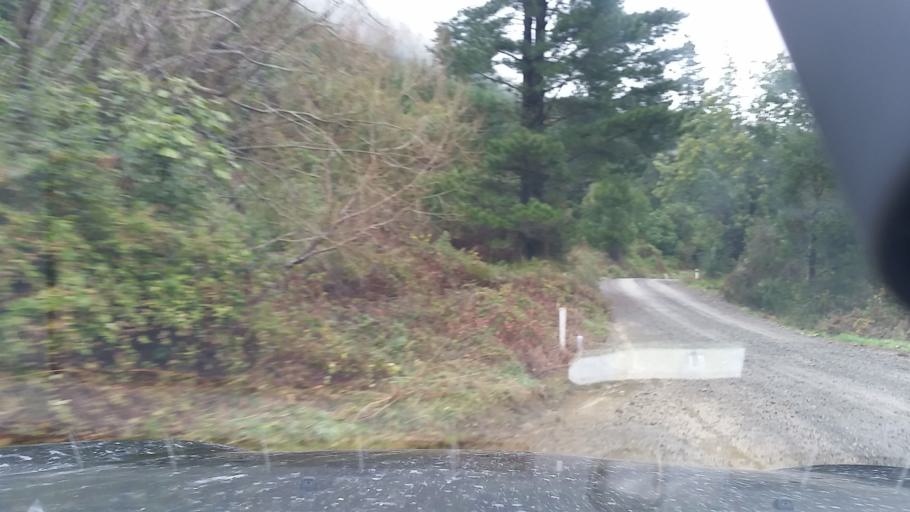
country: NZ
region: Nelson
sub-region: Nelson City
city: Nelson
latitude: -41.3588
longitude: 173.6204
